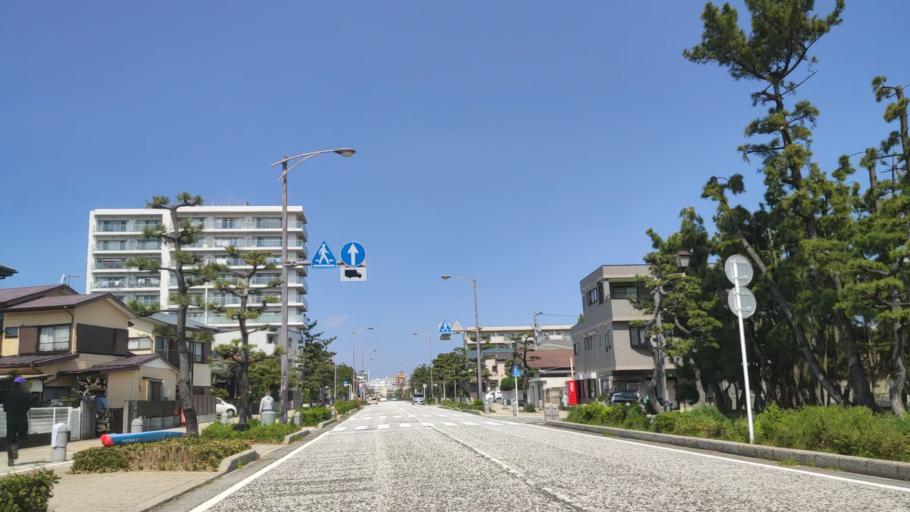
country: JP
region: Kanagawa
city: Hiratsuka
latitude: 35.3178
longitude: 139.3537
